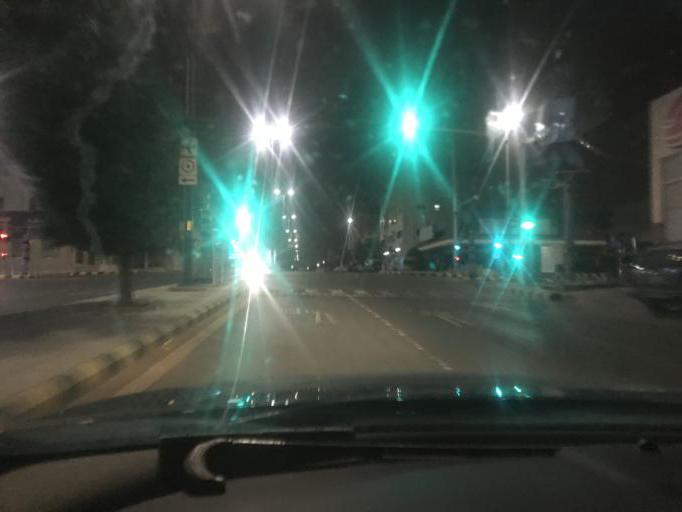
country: SA
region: Ar Riyad
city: Riyadh
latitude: 24.7308
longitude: 46.7624
